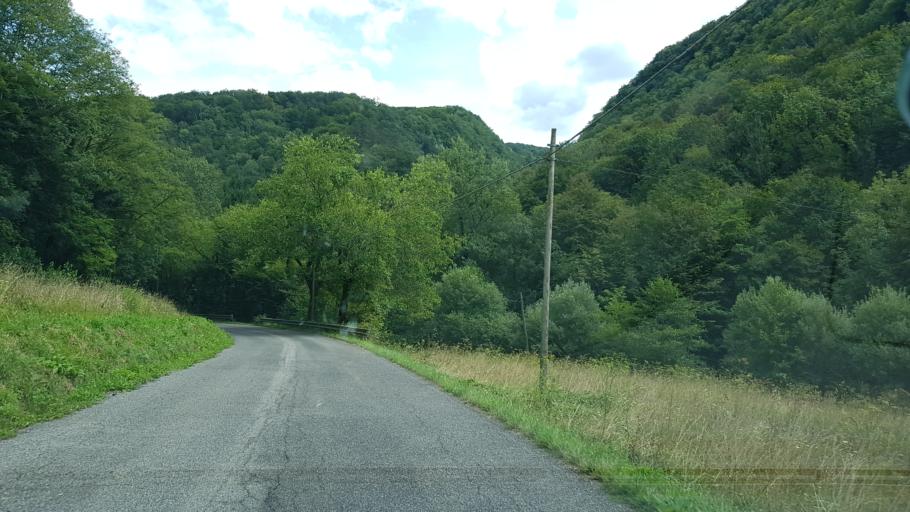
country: IT
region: Friuli Venezia Giulia
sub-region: Provincia di Udine
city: San Leonardo
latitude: 46.0844
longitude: 13.5535
